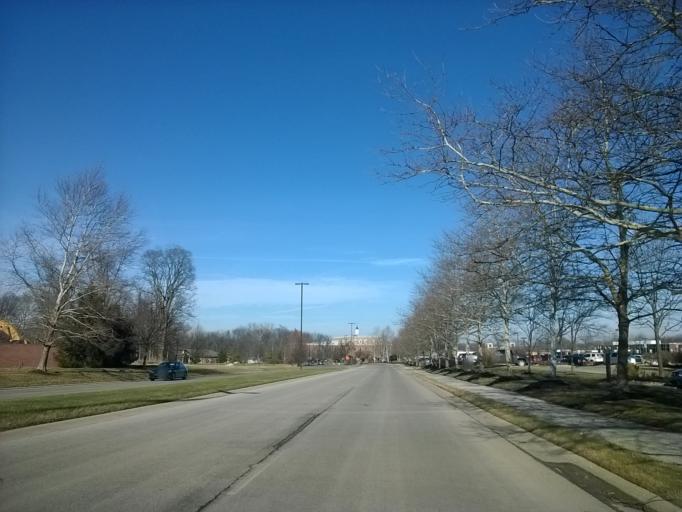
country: US
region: Indiana
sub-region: Marion County
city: Meridian Hills
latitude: 39.9392
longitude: -86.1603
